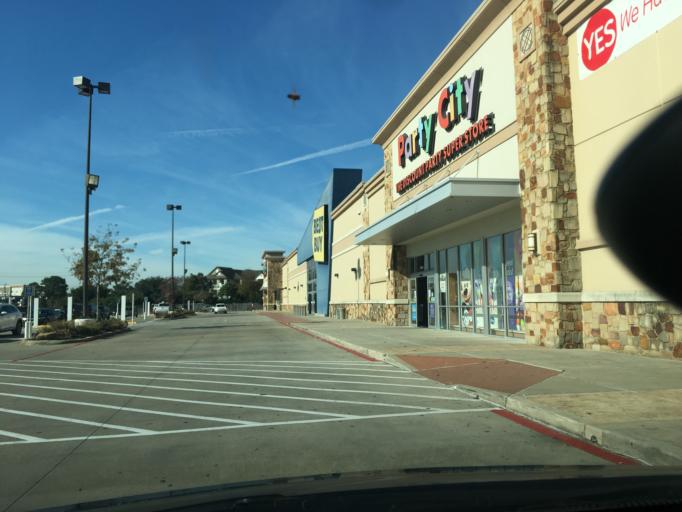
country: US
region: Texas
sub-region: Harris County
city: Cloverleaf
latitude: 29.8114
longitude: -95.1618
